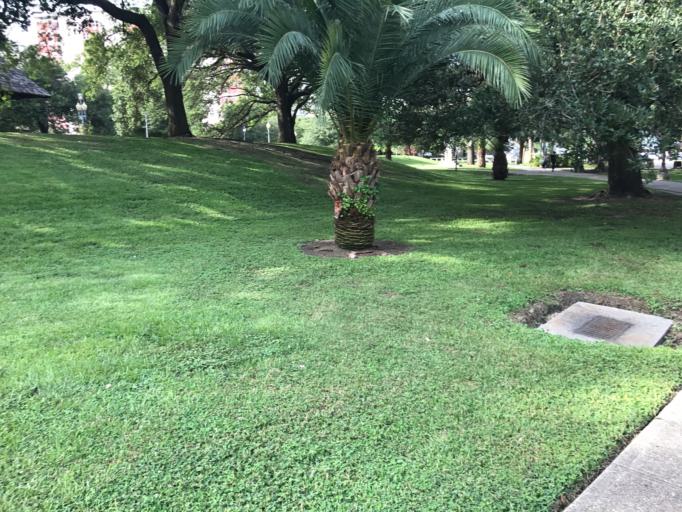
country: US
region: Louisiana
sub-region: Orleans Parish
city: New Orleans
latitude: 29.9526
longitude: -90.0762
